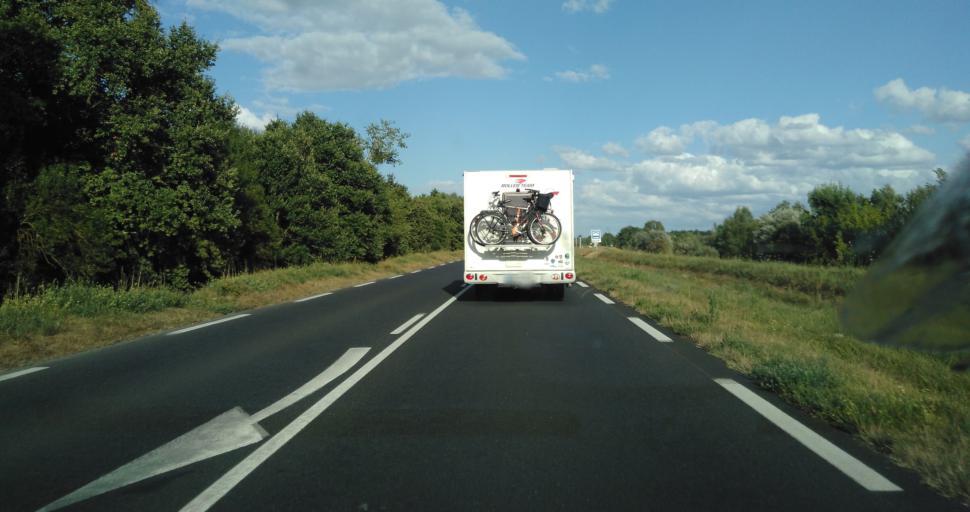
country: FR
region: Centre
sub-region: Departement d'Indre-et-Loire
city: Noizay
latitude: 47.4045
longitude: 0.8944
